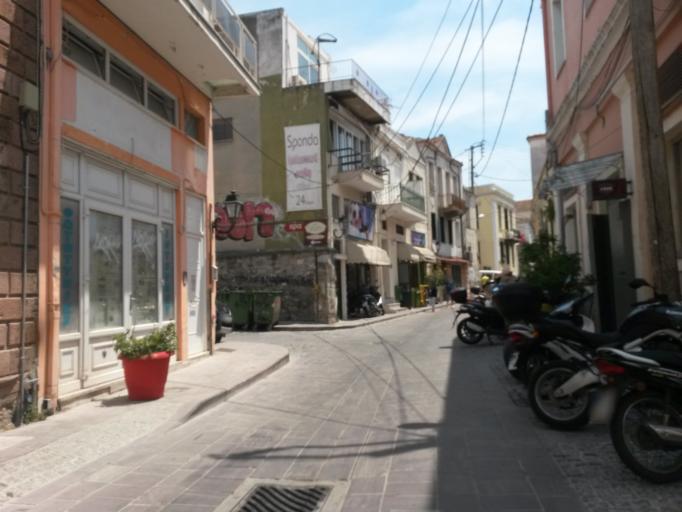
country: GR
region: North Aegean
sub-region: Nomos Lesvou
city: Mytilini
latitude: 39.1065
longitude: 26.5590
